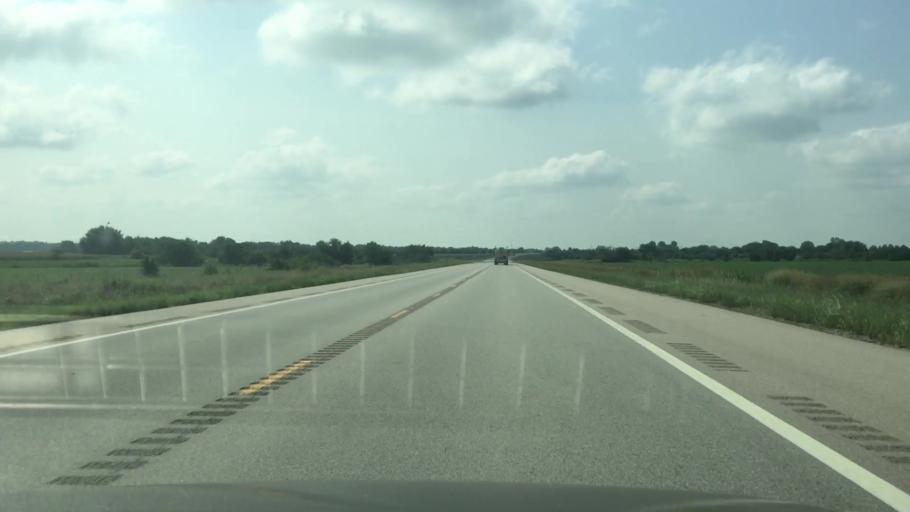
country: US
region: Kansas
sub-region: Allen County
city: Iola
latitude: 37.9470
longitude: -95.3805
